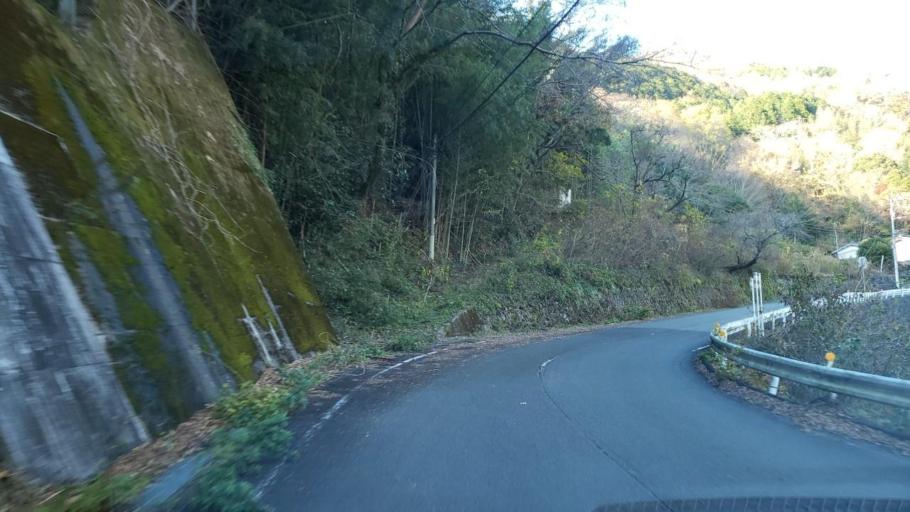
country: JP
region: Tokushima
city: Wakimachi
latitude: 34.0961
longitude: 134.0681
